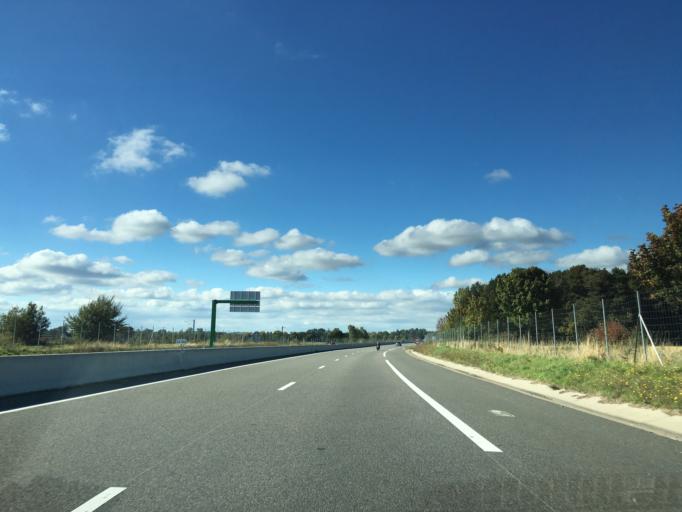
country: FR
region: Lorraine
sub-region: Departement de Meurthe-et-Moselle
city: Baccarat
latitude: 48.4688
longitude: 6.7306
